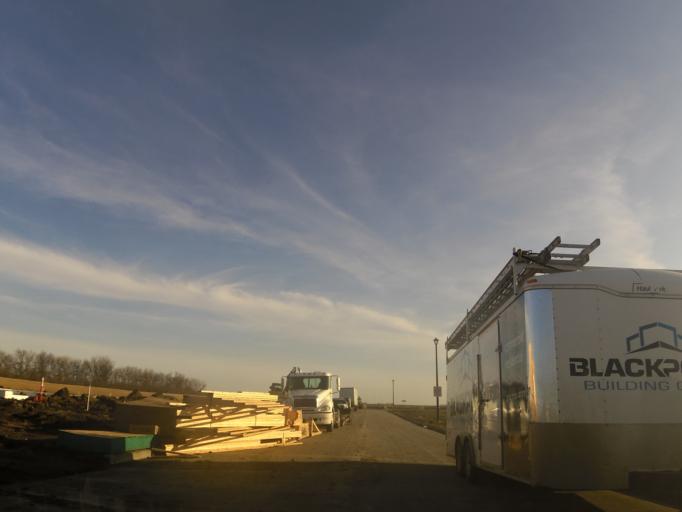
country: US
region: North Dakota
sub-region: Grand Forks County
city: Grand Forks
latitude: 47.8634
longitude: -97.0250
